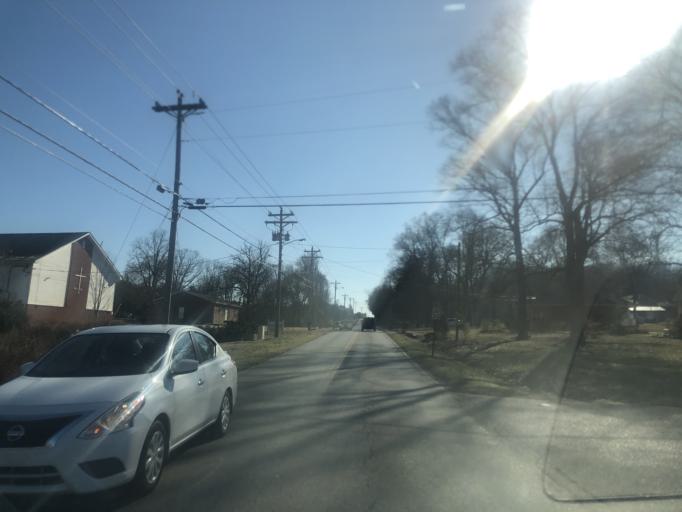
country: US
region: Tennessee
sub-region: Rutherford County
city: La Vergne
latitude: 35.9988
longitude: -86.5594
